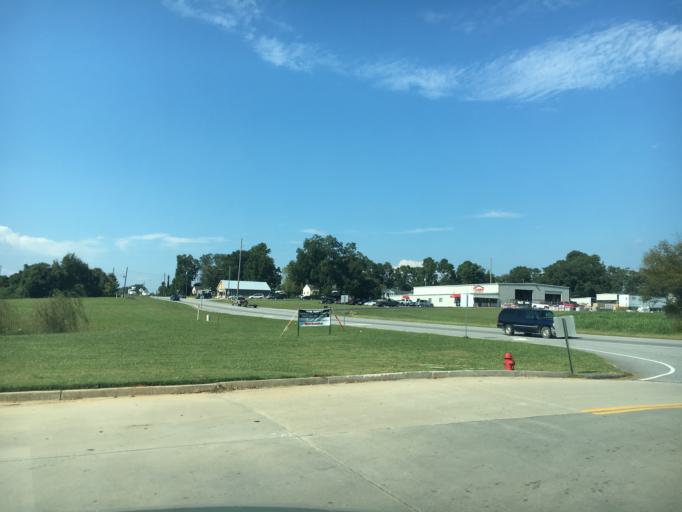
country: US
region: Georgia
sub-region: Franklin County
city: Lavonia
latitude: 34.4203
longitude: -83.1021
